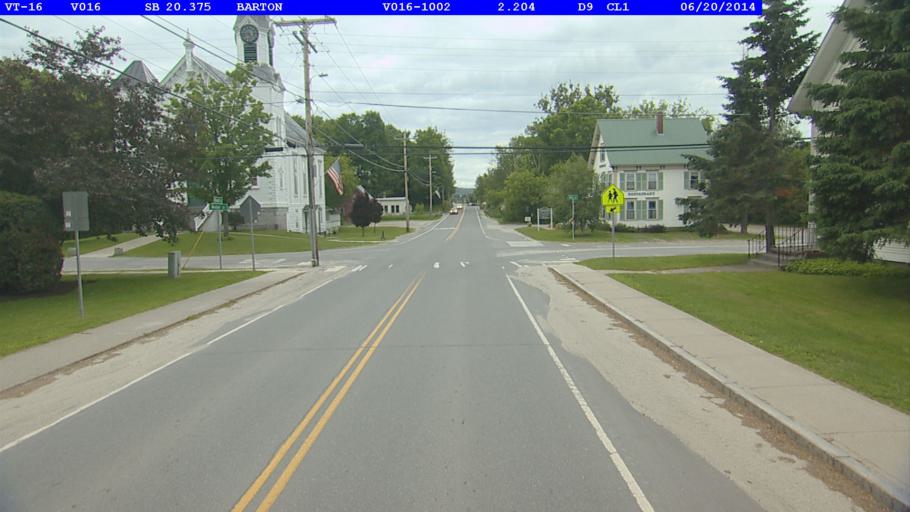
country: US
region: Vermont
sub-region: Orleans County
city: Newport
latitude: 44.7487
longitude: -72.1805
